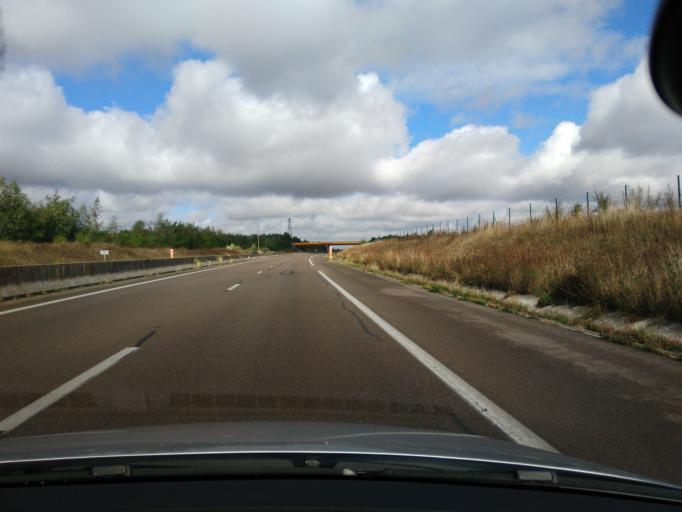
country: FR
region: Haute-Normandie
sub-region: Departement de l'Eure
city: La Madeleine-de-Nonancourt
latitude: 48.8320
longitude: 1.1850
